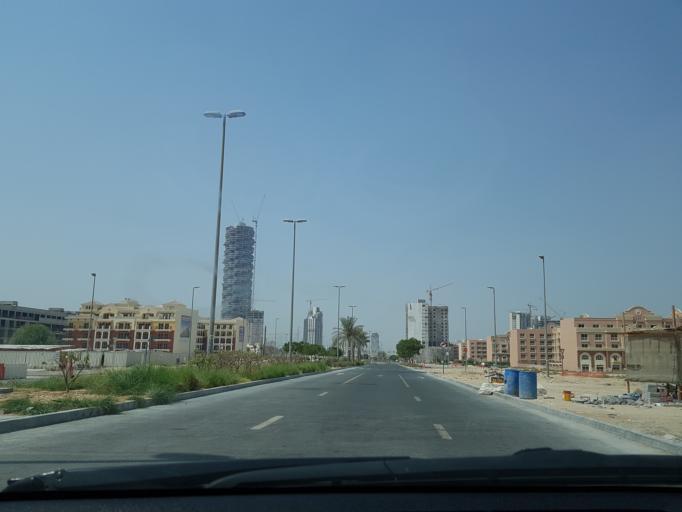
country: AE
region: Dubai
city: Dubai
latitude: 25.0500
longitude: 55.2164
